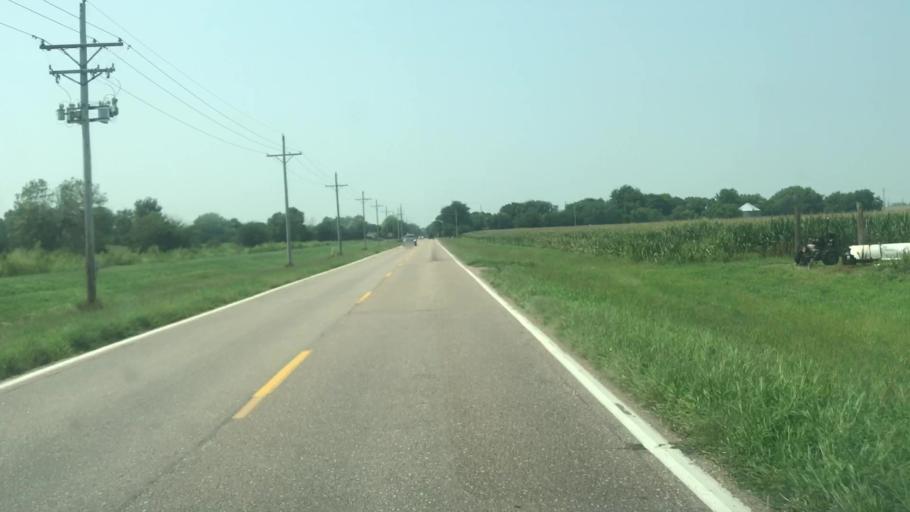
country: US
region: Nebraska
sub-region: Hall County
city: Grand Island
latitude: 40.9164
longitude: -98.3155
